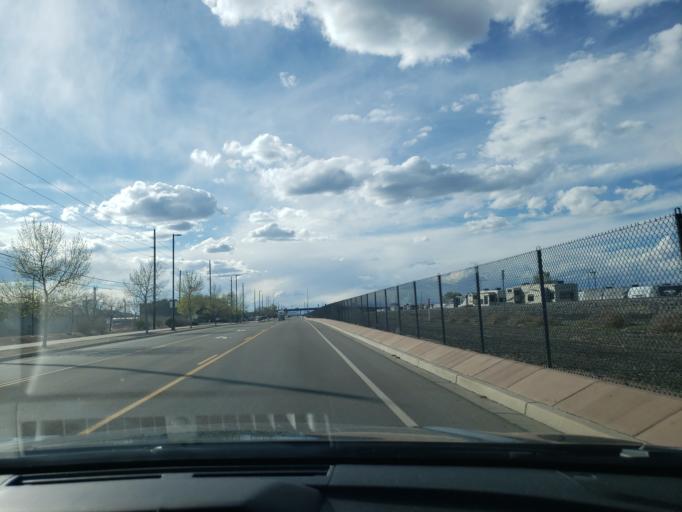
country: US
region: Colorado
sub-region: Mesa County
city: Redlands
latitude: 39.0873
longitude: -108.6019
